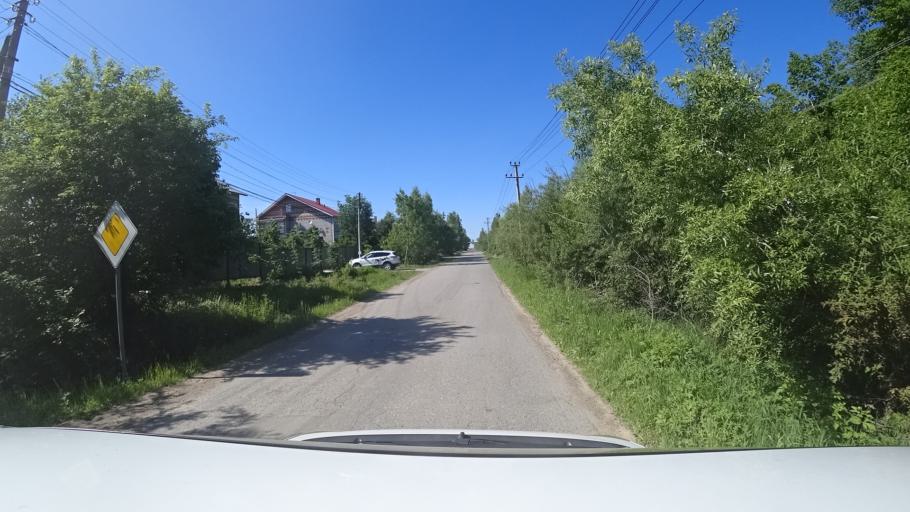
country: RU
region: Khabarovsk Krai
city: Topolevo
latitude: 48.5476
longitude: 135.1743
